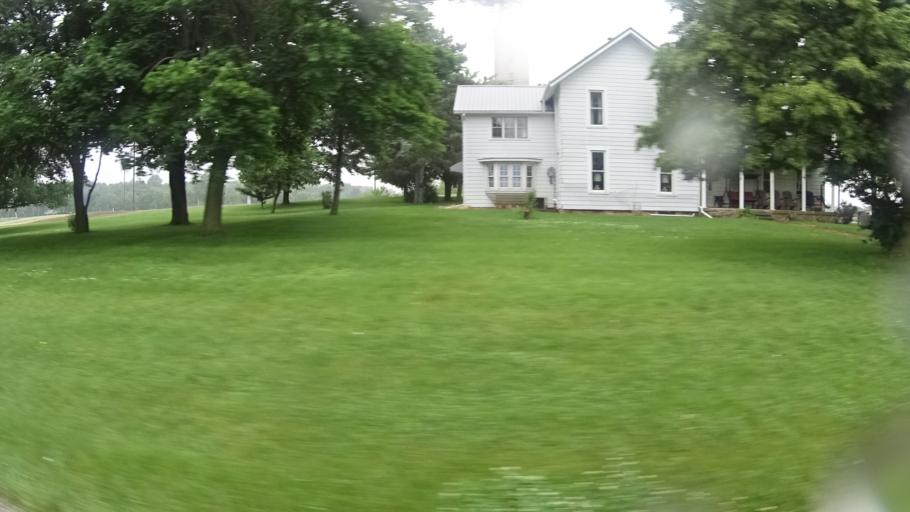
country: US
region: Ohio
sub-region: Huron County
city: Bellevue
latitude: 41.3412
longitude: -82.8421
